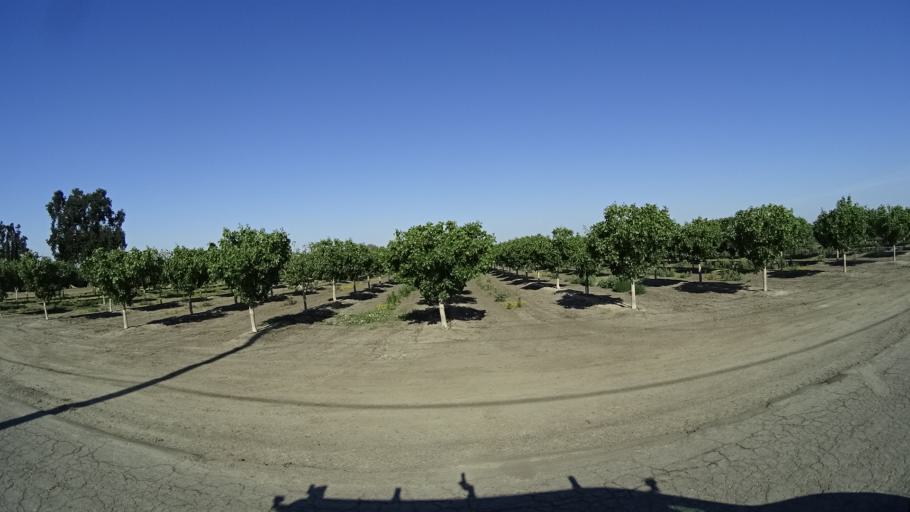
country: US
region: California
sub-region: Kings County
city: Corcoran
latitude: 36.1171
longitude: -119.5543
